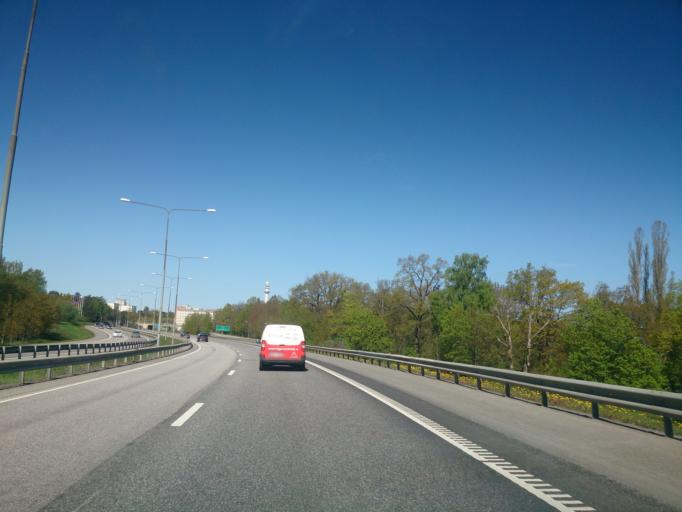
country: SE
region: Stockholm
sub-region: Nacka Kommun
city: Alta
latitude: 59.2428
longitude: 18.1159
